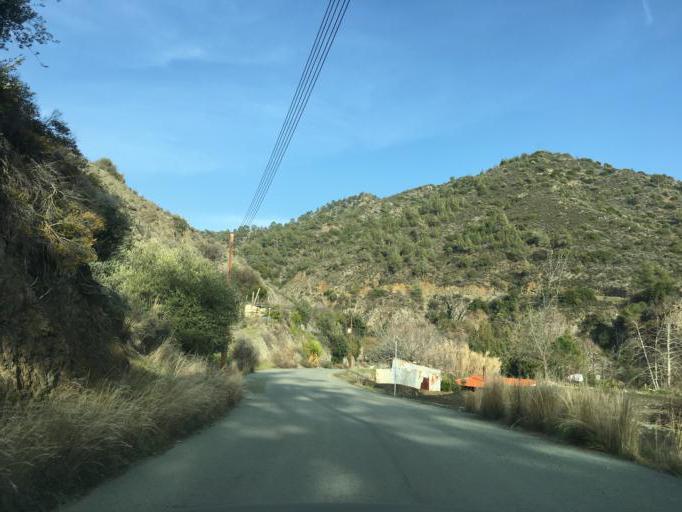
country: CY
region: Limassol
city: Pelendri
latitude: 34.8295
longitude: 32.9657
